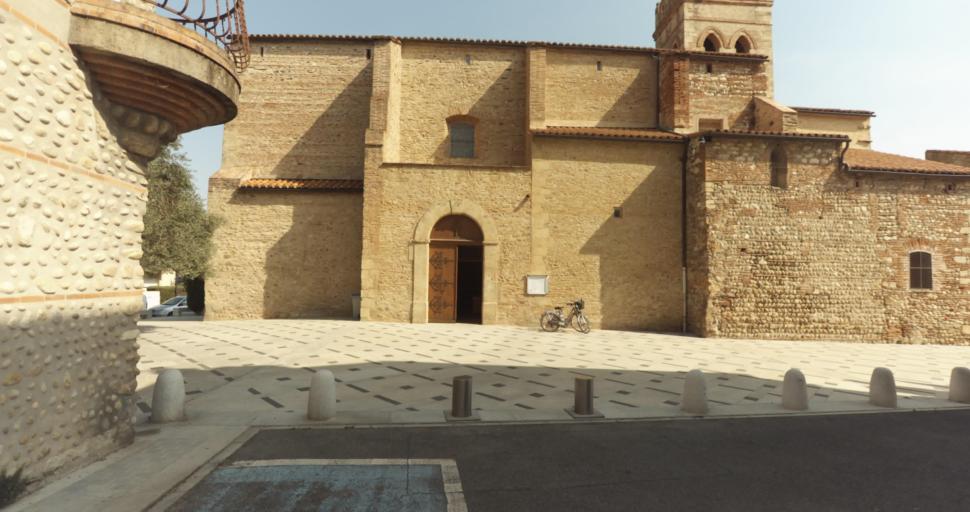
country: FR
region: Languedoc-Roussillon
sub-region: Departement des Pyrenees-Orientales
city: Latour-Bas-Elne
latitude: 42.6174
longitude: 3.0008
